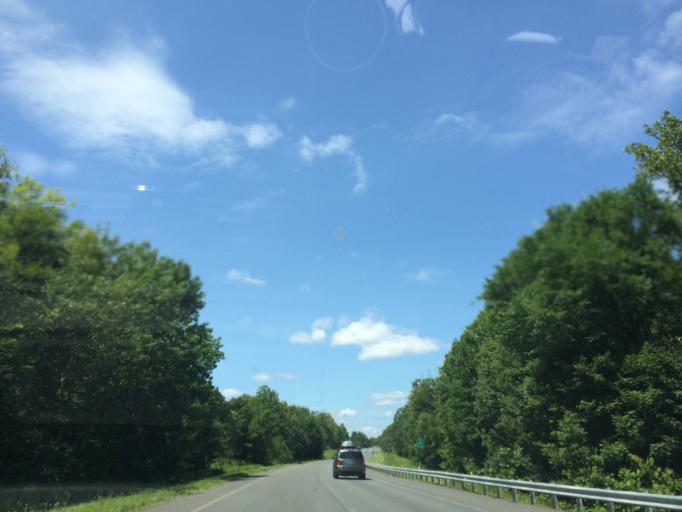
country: US
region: Pennsylvania
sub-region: Wayne County
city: Hawley
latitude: 41.3512
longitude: -75.2424
